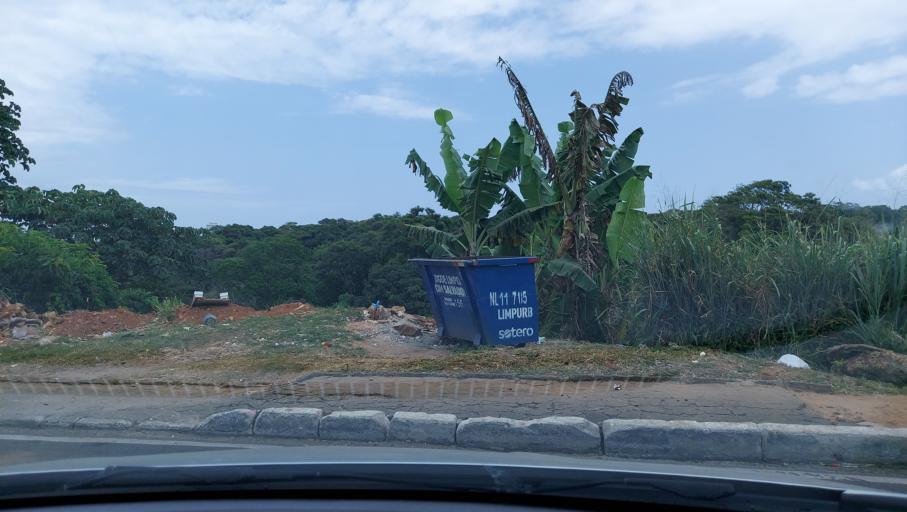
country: BR
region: Bahia
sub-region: Salvador
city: Salvador
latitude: -12.9631
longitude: -38.4444
